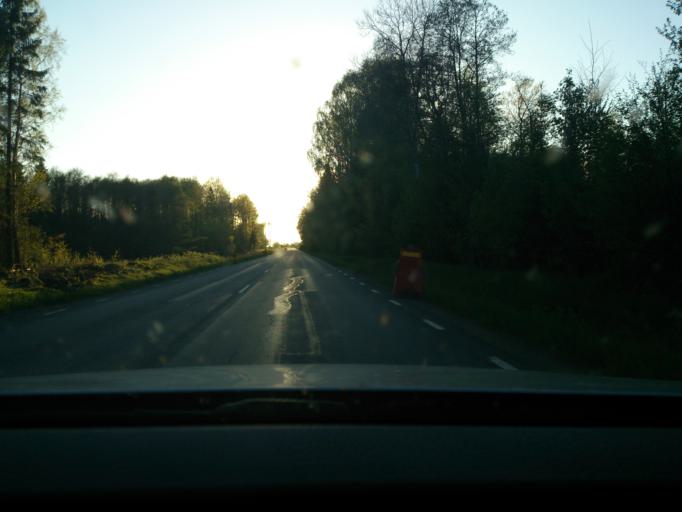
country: SE
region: Kronoberg
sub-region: Alvesta Kommun
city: Moheda
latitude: 56.9881
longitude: 14.6042
